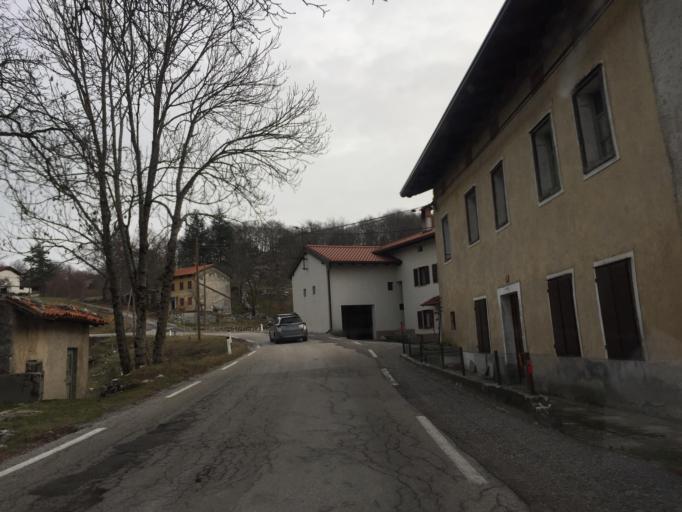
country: SI
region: Nova Gorica
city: Sempas
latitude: 45.9746
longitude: 13.7438
